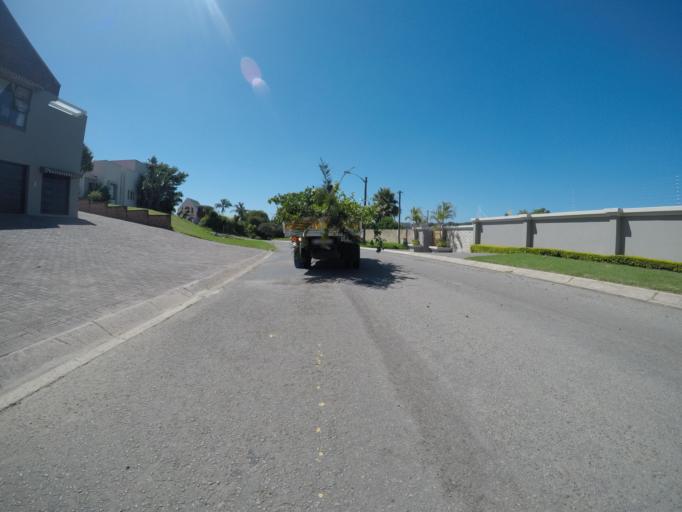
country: ZA
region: Eastern Cape
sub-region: Buffalo City Metropolitan Municipality
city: East London
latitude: -32.9805
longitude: 27.9345
